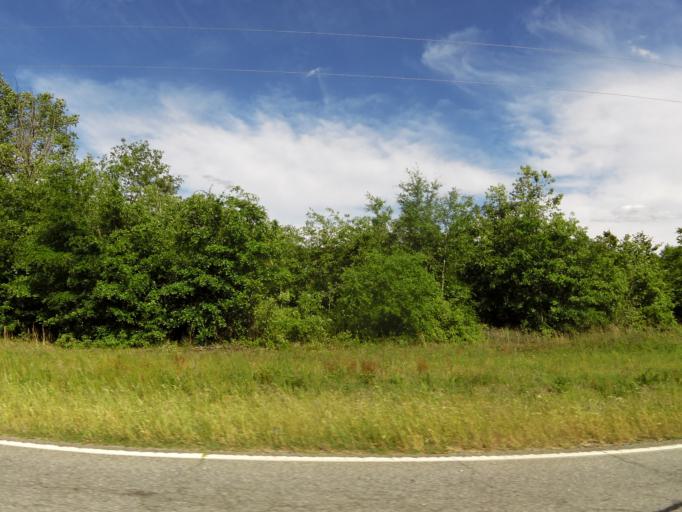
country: US
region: South Carolina
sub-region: Bamberg County
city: Denmark
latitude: 33.2017
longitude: -81.1773
